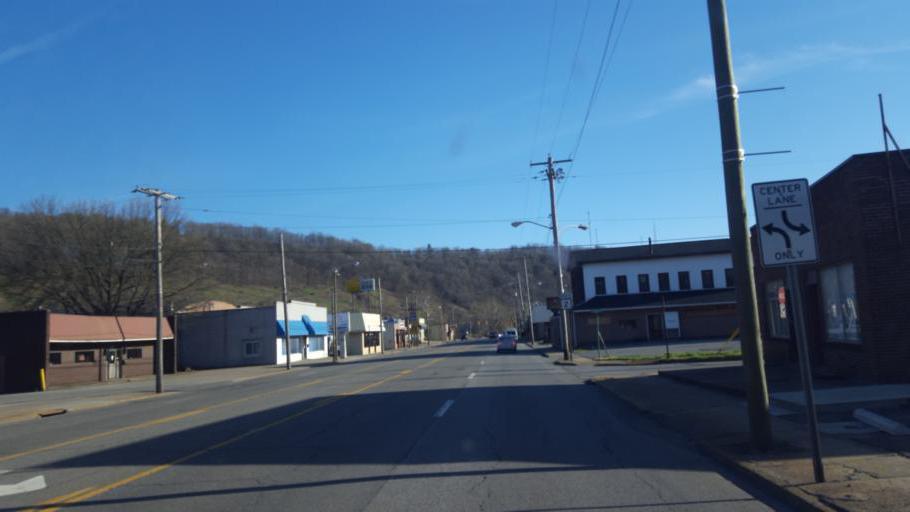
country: US
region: West Virginia
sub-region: Hancock County
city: Weirton
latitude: 40.3959
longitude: -80.5920
